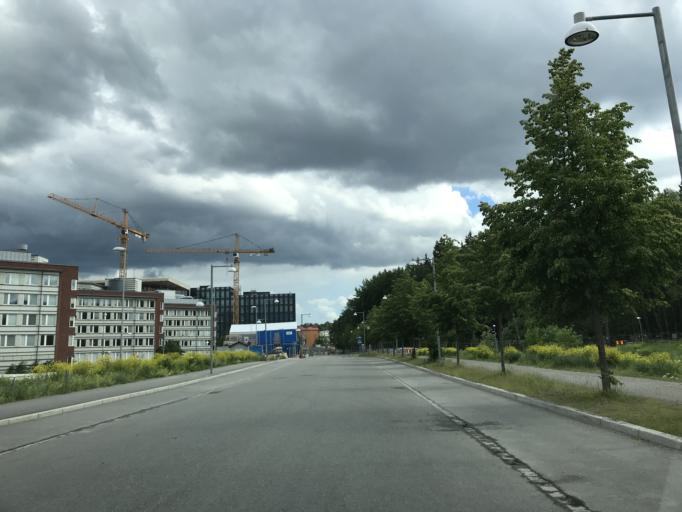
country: SE
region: Stockholm
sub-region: Solna Kommun
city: Solna
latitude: 59.3802
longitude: 18.0058
